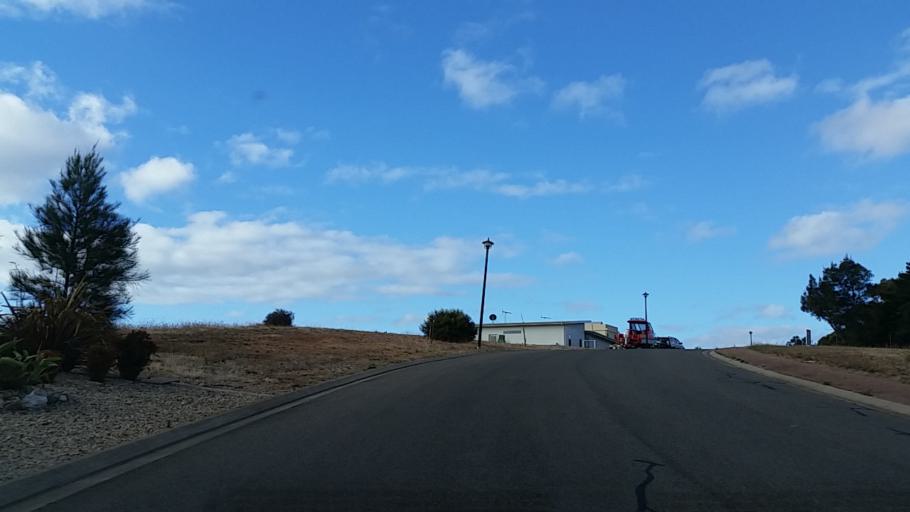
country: AU
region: South Australia
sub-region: Yankalilla
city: Normanville
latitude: -35.5050
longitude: 138.2459
